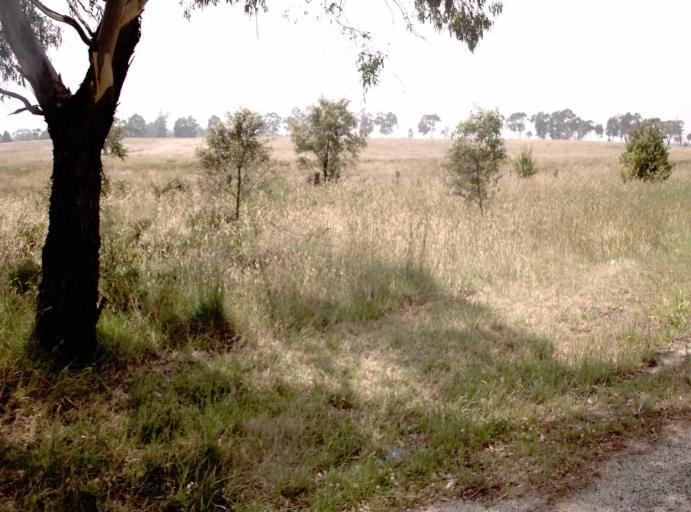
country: AU
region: Victoria
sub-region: Latrobe
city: Traralgon
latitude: -38.2474
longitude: 146.6510
